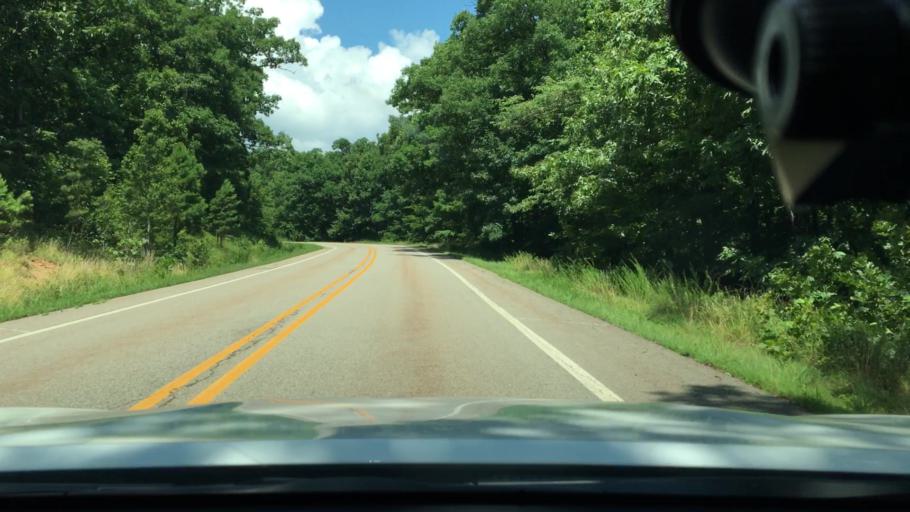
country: US
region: Arkansas
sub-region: Logan County
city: Paris
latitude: 35.1700
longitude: -93.6419
